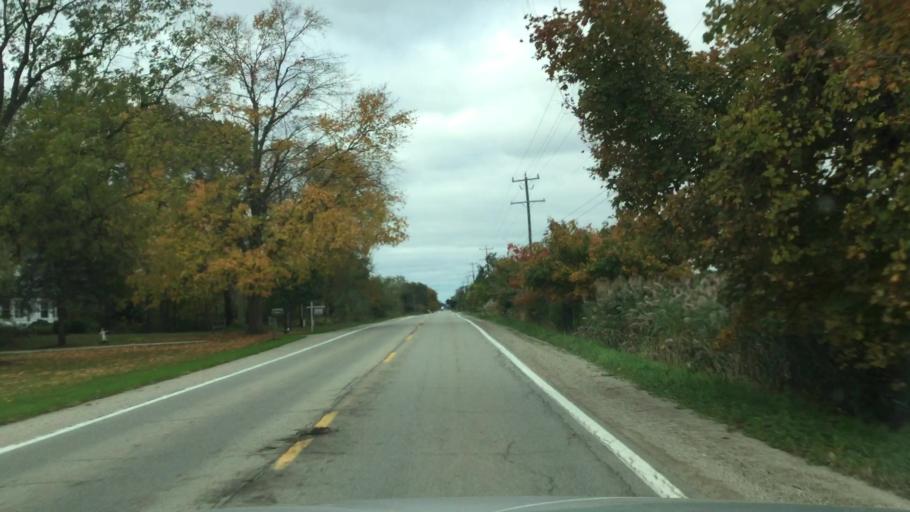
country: US
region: Michigan
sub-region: Macomb County
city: Armada
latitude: 42.8060
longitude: -82.9065
